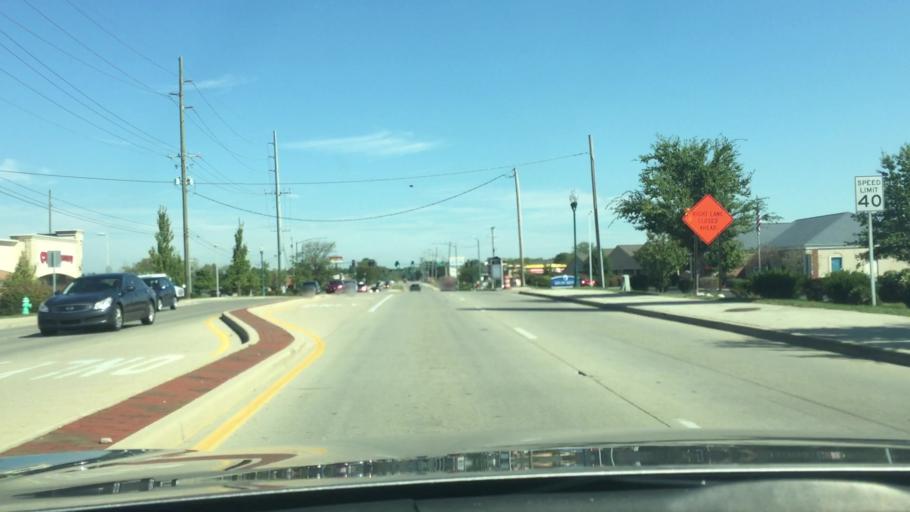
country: US
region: Indiana
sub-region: Hamilton County
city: Fishers
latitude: 39.9550
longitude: -86.0406
